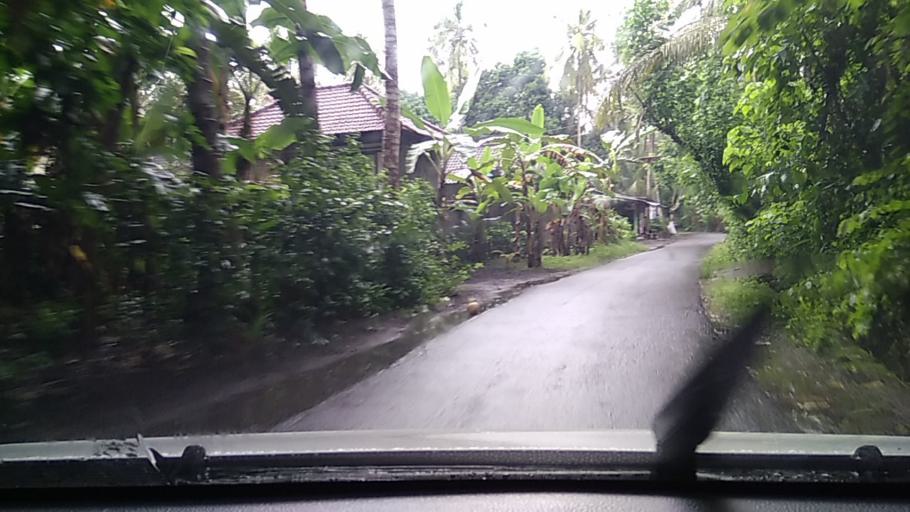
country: ID
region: Bali
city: Banjar Bugbug
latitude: -8.5114
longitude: 115.5787
